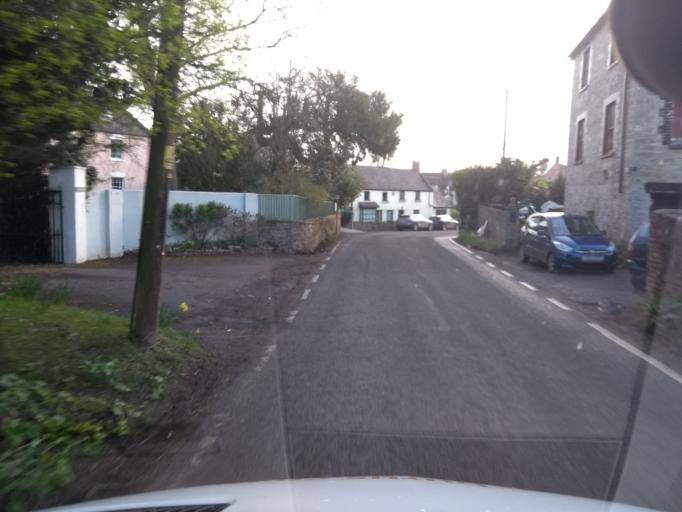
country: GB
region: England
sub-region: Somerset
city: Wedmore
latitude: 51.2135
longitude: -2.7746
